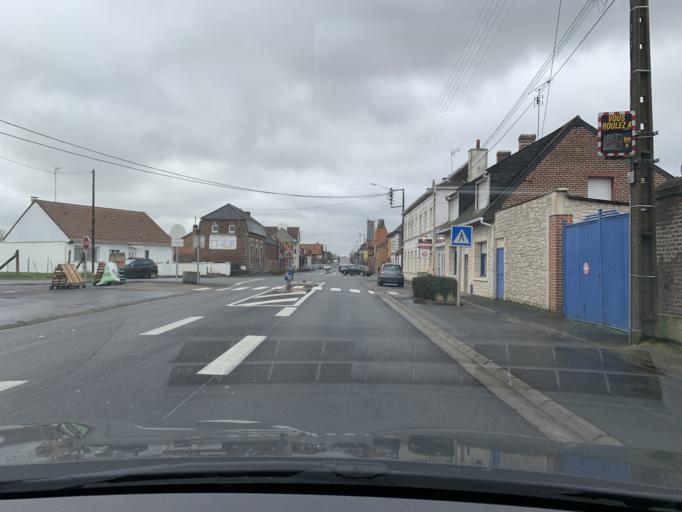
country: FR
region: Nord-Pas-de-Calais
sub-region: Departement du Nord
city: Iwuy
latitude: 50.2398
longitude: 3.3214
